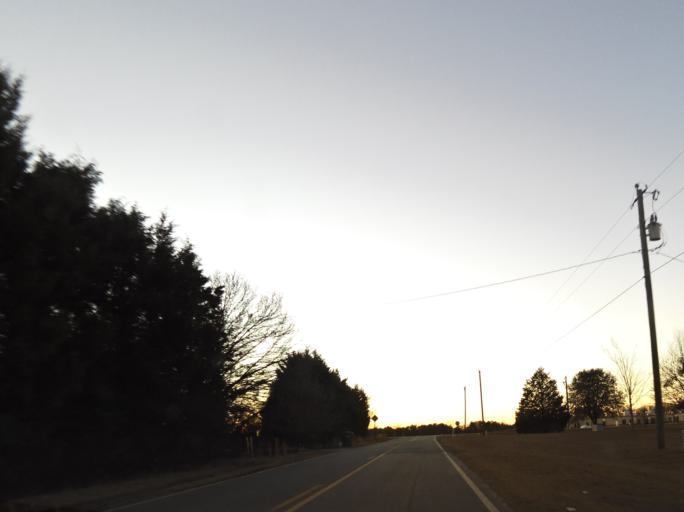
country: US
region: Georgia
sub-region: Peach County
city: Byron
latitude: 32.6038
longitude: -83.7564
